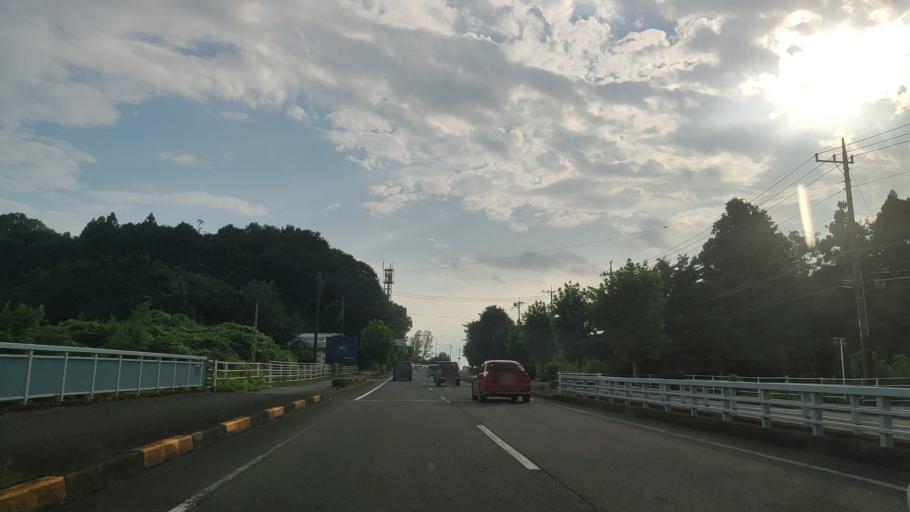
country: JP
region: Tochigi
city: Utsunomiya-shi
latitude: 36.5481
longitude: 139.8334
